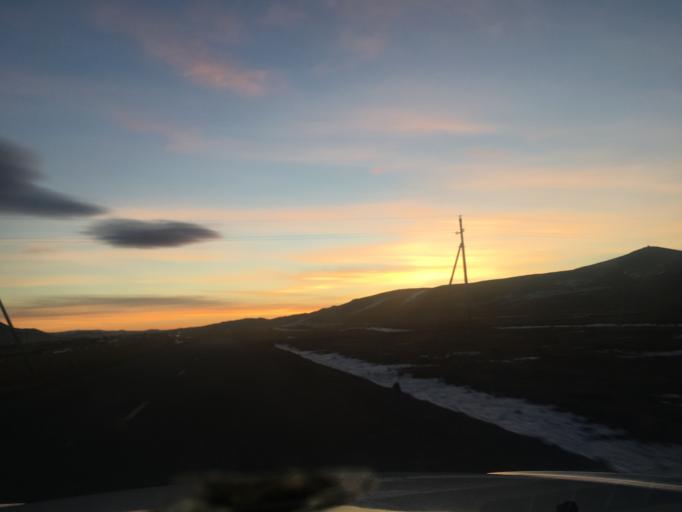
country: MN
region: Central Aimak
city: Mandal
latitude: 48.1086
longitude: 106.6332
